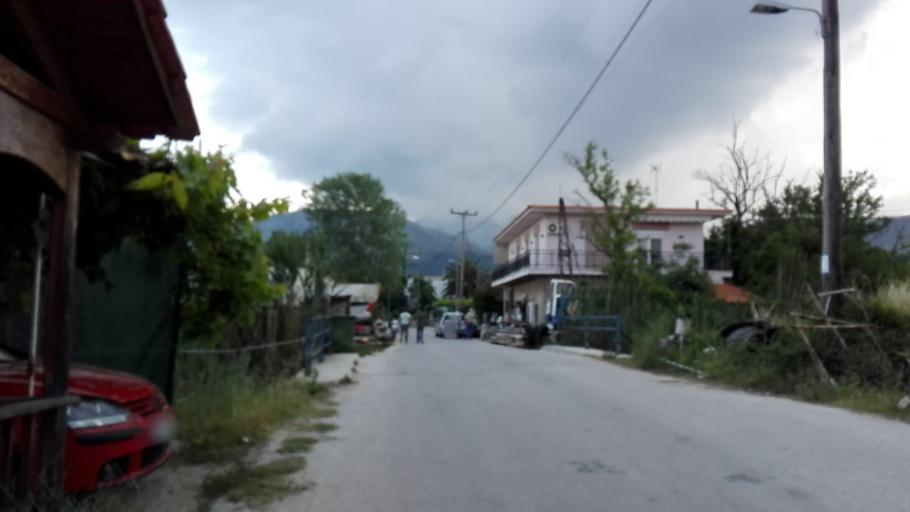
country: GR
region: East Macedonia and Thrace
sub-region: Nomos Kavalas
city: Prinos
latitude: 40.7592
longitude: 24.5736
